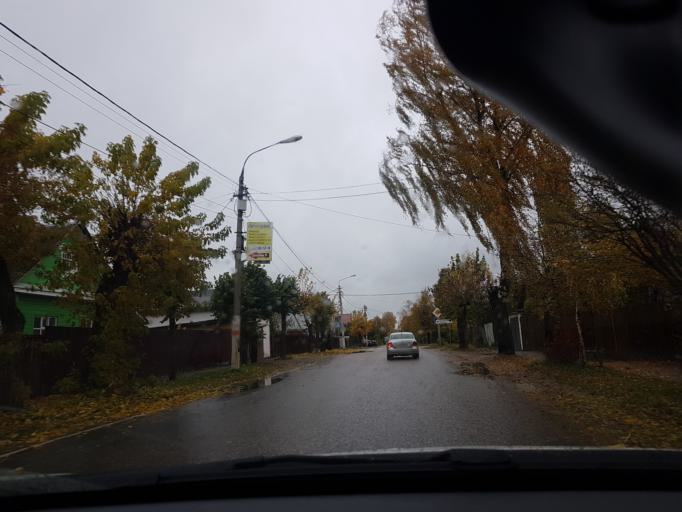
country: RU
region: Moskovskaya
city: Istra
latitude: 55.9153
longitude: 36.8677
